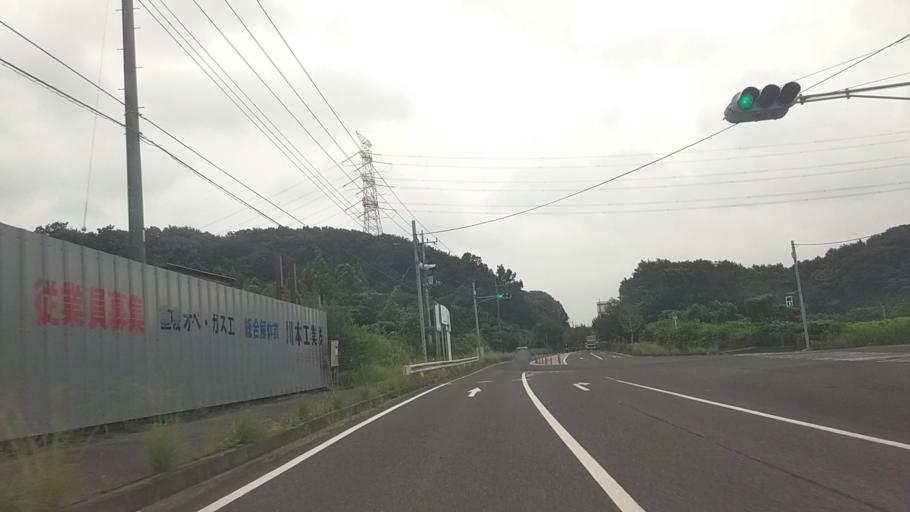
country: JP
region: Chiba
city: Kisarazu
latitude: 35.3865
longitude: 140.0009
